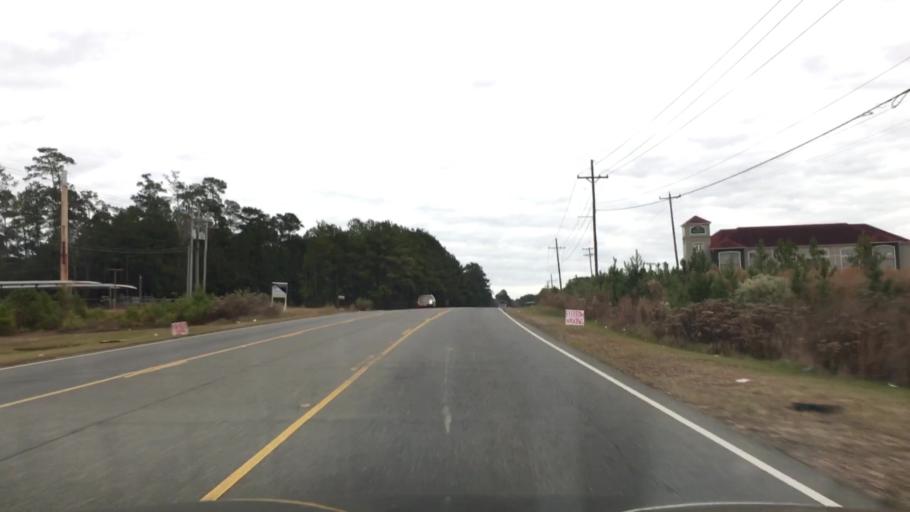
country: US
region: Louisiana
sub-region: Vernon Parish
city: Fort Polk South
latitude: 31.0549
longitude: -93.2414
